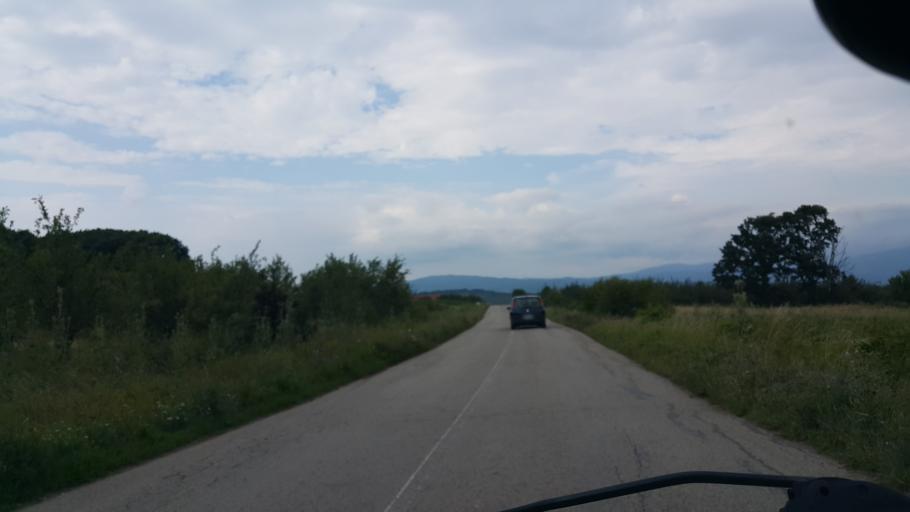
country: RS
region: Central Serbia
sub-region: Toplicki Okrug
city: Blace
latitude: 43.2643
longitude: 21.2728
